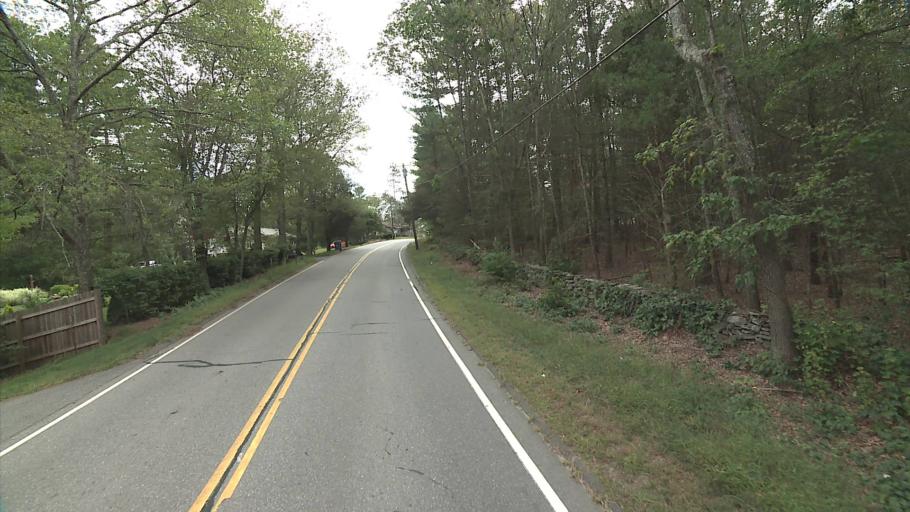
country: US
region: Connecticut
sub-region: New London County
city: Jewett City
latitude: 41.6385
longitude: -71.9555
